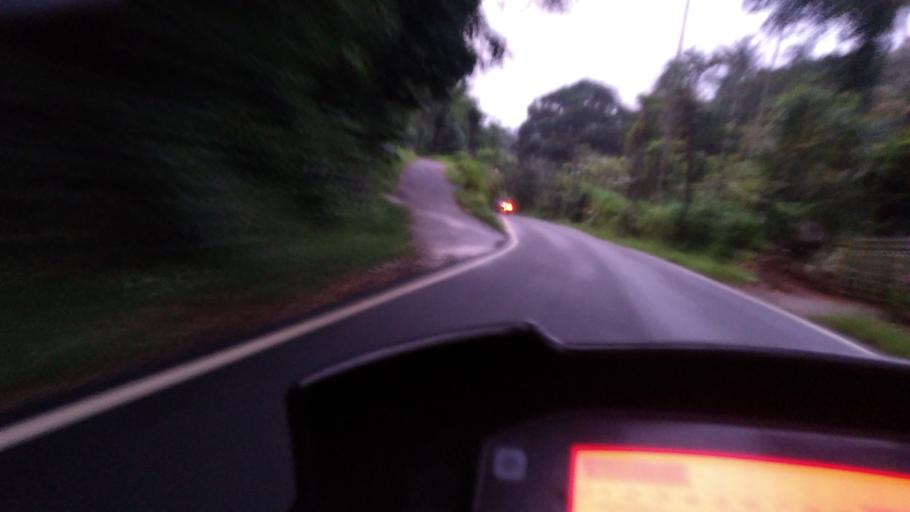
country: IN
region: Kerala
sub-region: Idukki
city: Munnar
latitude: 9.9590
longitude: 77.0756
